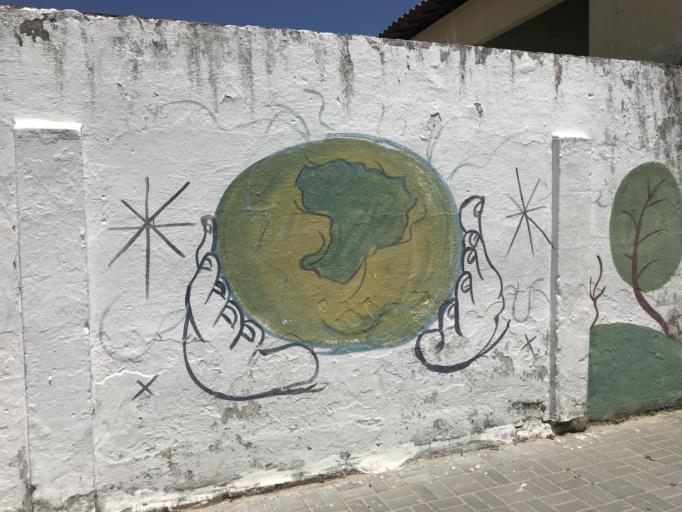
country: BR
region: Ceara
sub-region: Fortaleza
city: Fortaleza
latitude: -3.7191
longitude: -38.5470
